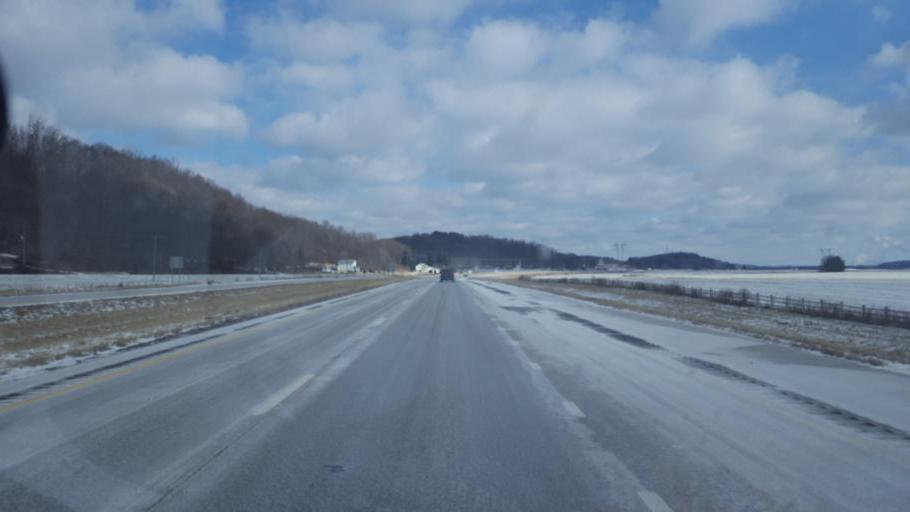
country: US
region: Ohio
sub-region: Muskingum County
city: Frazeysburg
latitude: 40.1055
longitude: -82.1738
